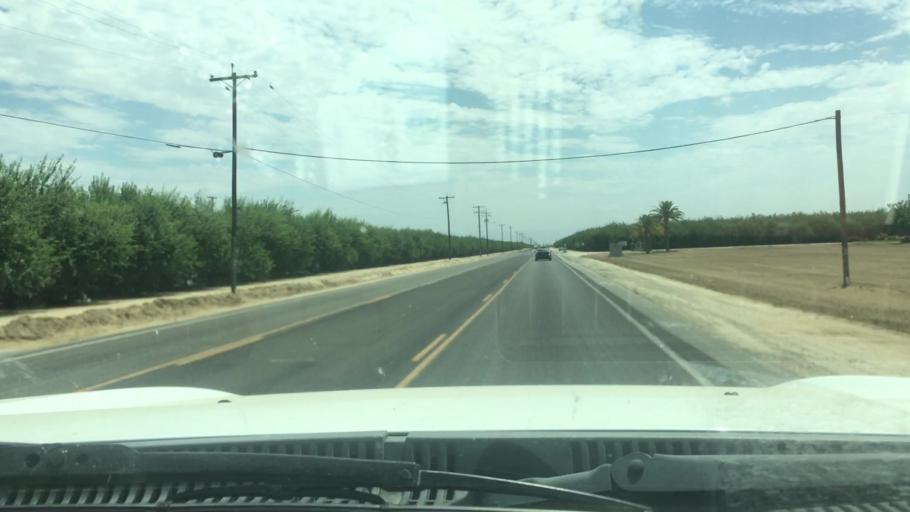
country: US
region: California
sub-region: Kern County
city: Wasco
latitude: 35.5580
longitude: -119.3242
